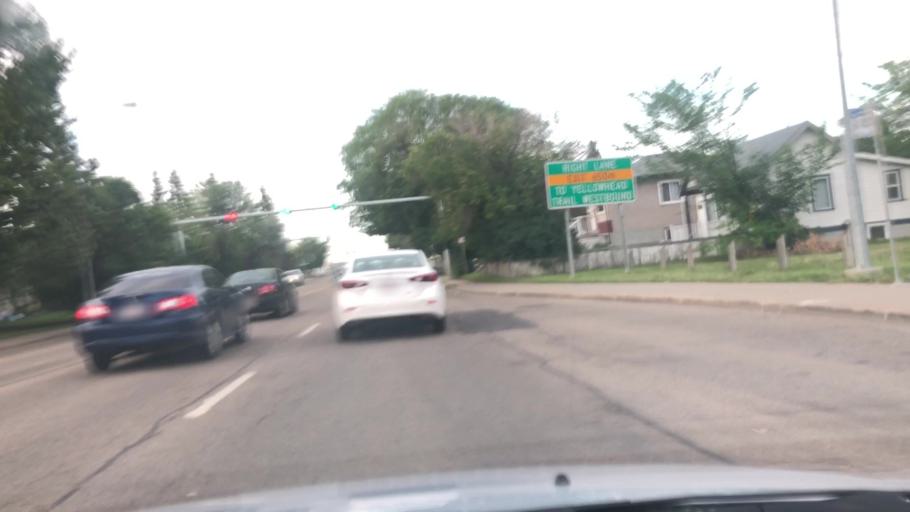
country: CA
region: Alberta
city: Edmonton
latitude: 53.5872
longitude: -113.5413
